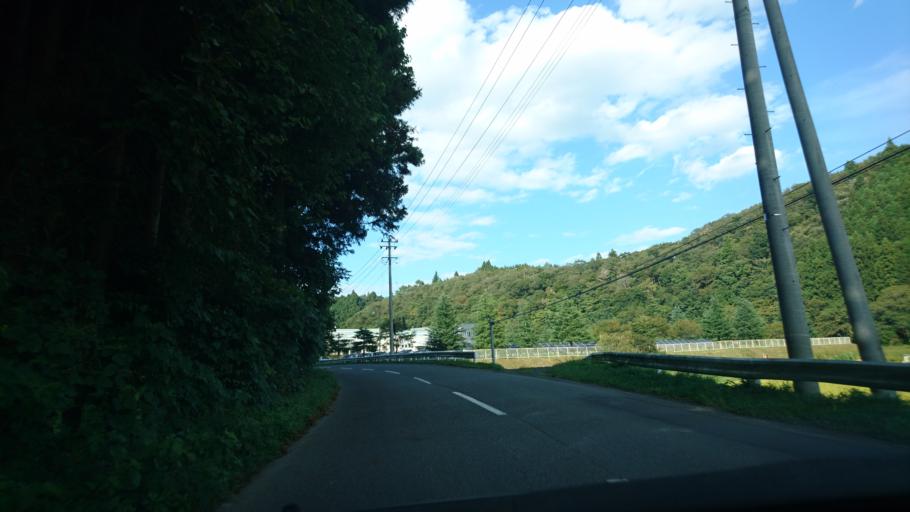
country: JP
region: Iwate
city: Ichinoseki
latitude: 38.8519
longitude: 141.3031
